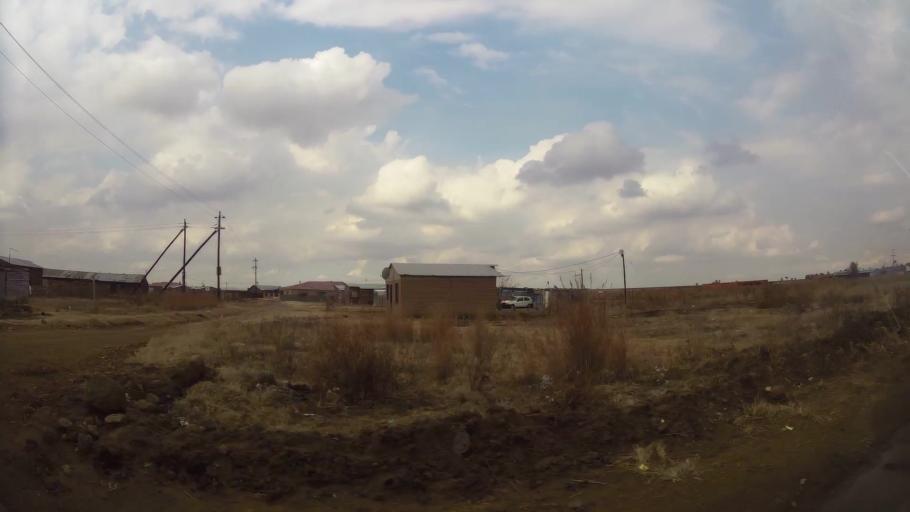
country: ZA
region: Orange Free State
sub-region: Fezile Dabi District Municipality
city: Sasolburg
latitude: -26.8658
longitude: 27.8944
